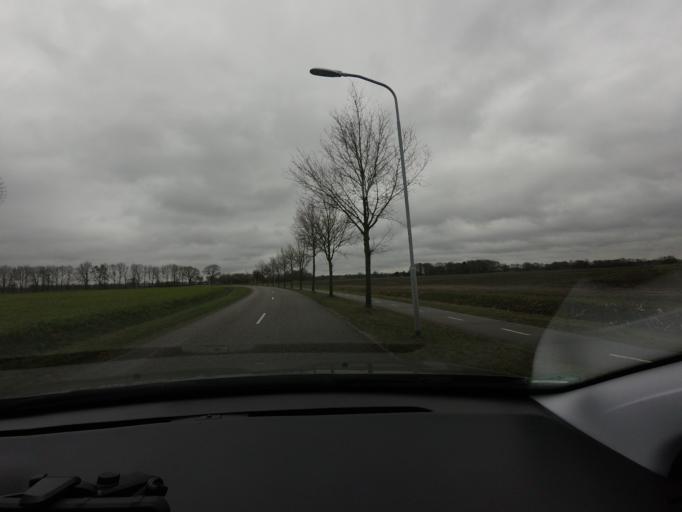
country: NL
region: Drenthe
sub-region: Gemeente Hoogeveen
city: Hoogeveen
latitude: 52.8364
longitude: 6.5319
